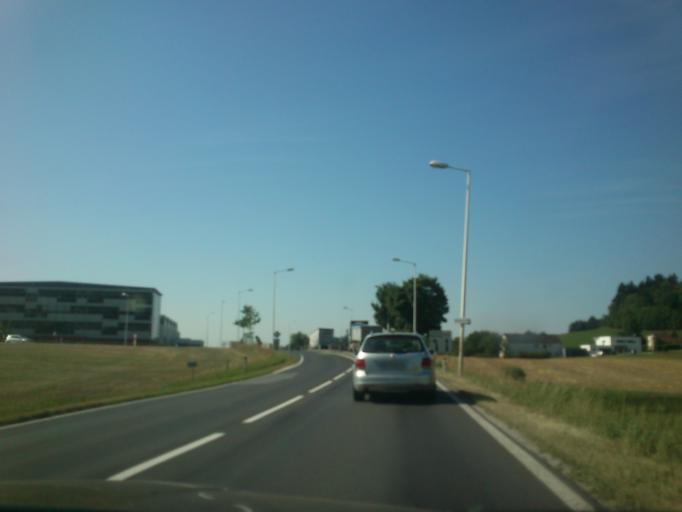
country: AT
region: Upper Austria
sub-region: Politischer Bezirk Urfahr-Umgebung
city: Alberndorf in der Riedmark
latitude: 48.4065
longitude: 14.4897
